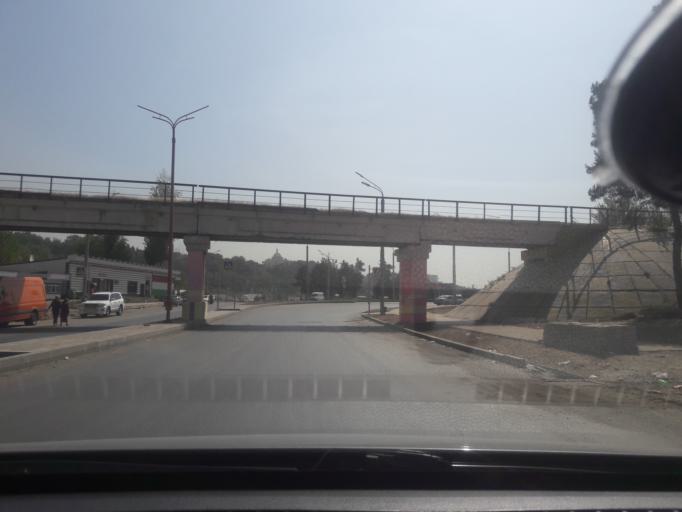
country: TJ
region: Dushanbe
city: Dushanbe
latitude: 38.6032
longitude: 68.7743
